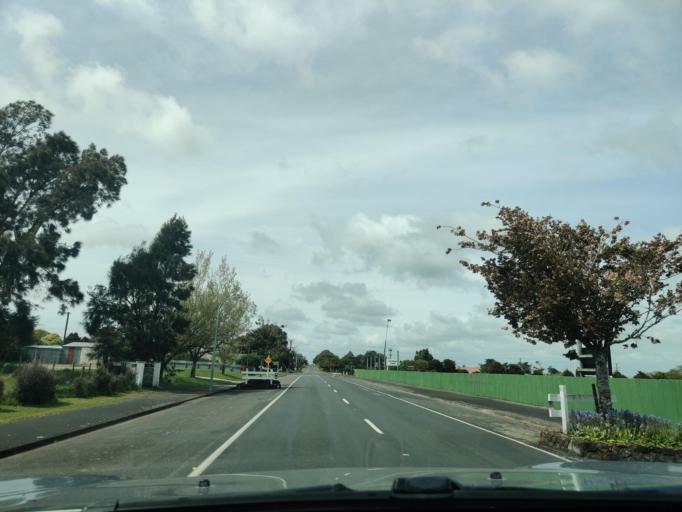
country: NZ
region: Taranaki
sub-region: South Taranaki District
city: Eltham
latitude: -39.4290
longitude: 174.1515
